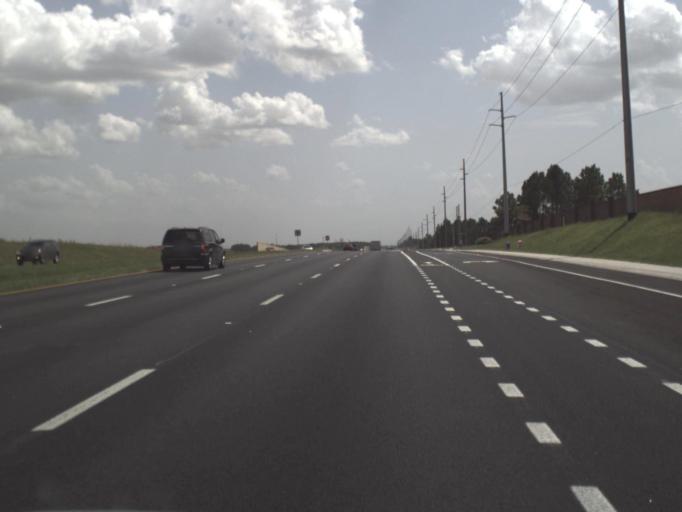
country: US
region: Florida
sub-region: Lake County
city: Four Corners
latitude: 28.2826
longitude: -81.6633
